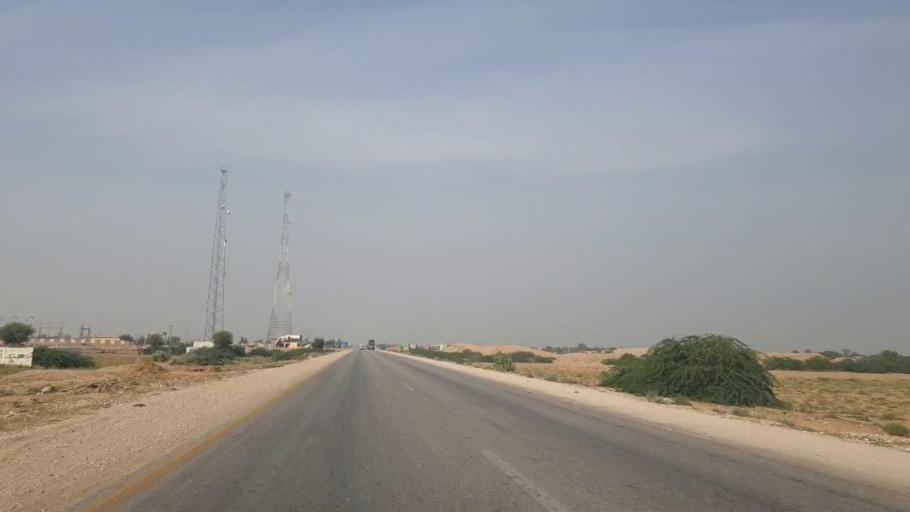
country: PK
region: Sindh
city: Sann
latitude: 26.0520
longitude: 68.1077
